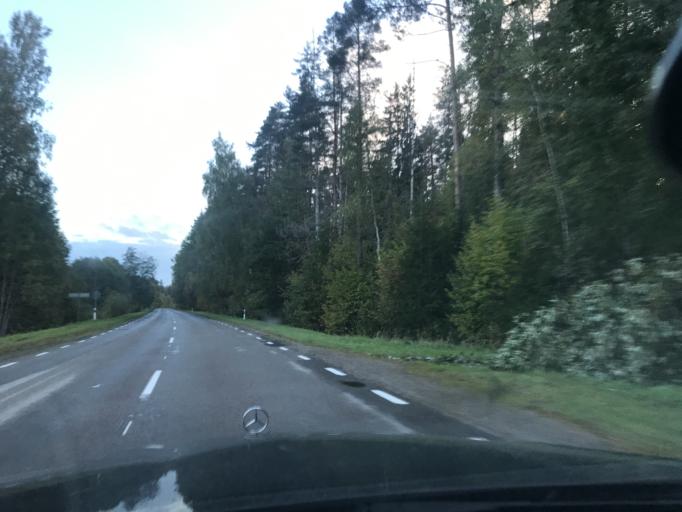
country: EE
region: Valgamaa
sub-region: Torva linn
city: Torva
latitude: 58.0028
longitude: 26.0805
